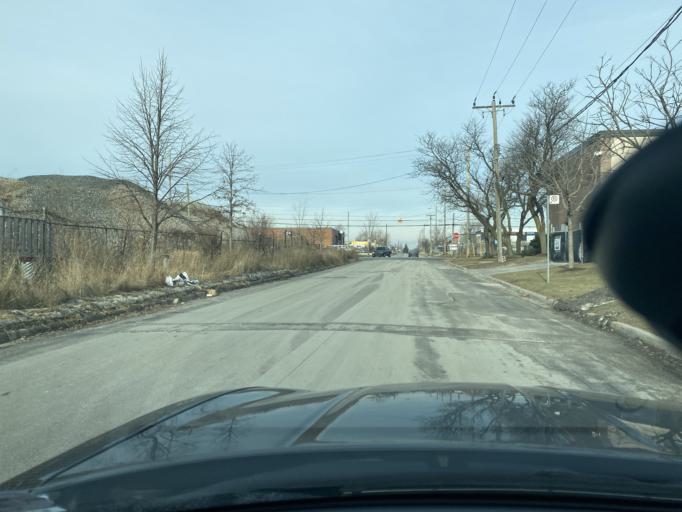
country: CA
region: Ontario
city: Scarborough
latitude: 43.7217
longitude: -79.2814
